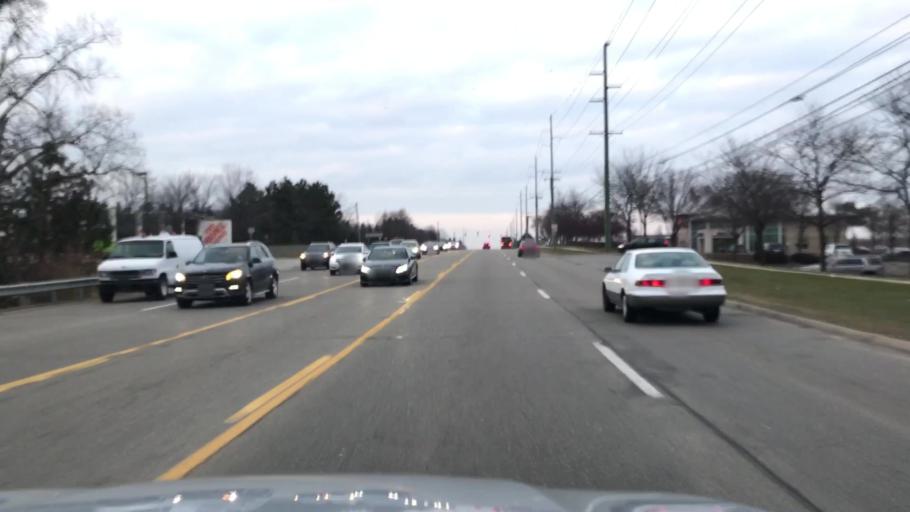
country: US
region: Michigan
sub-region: Wayne County
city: Northville
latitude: 42.4260
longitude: -83.4330
